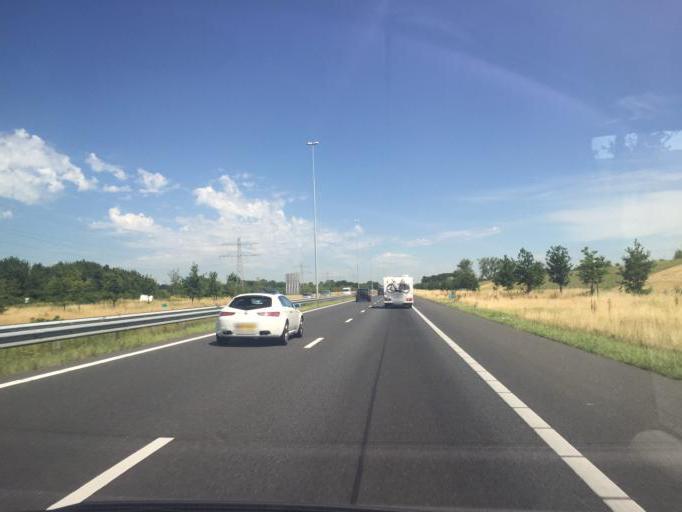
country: NL
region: North Brabant
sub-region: Gemeente Cuijk
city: Cuijk
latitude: 51.7421
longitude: 5.8424
